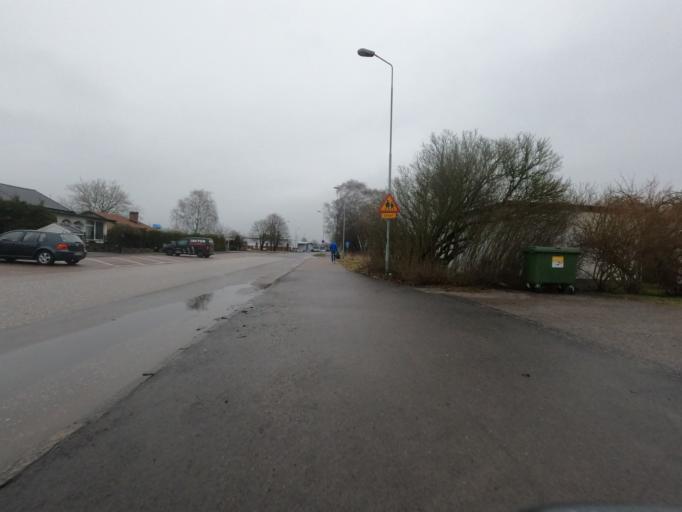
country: SE
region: Halland
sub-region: Halmstads Kommun
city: Halmstad
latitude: 56.6726
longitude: 12.8869
